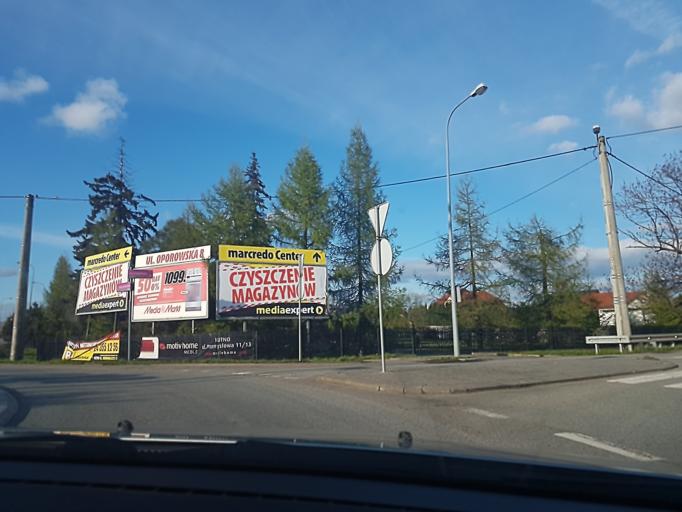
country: PL
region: Lodz Voivodeship
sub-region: Powiat kutnowski
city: Kutno
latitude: 52.2272
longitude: 19.3869
